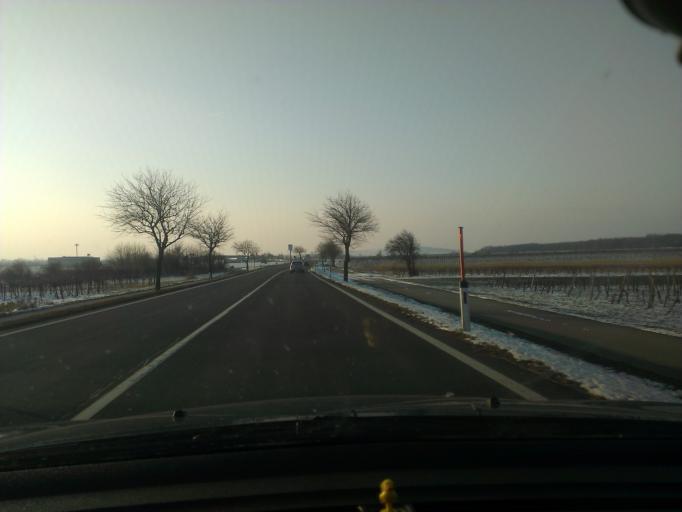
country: AT
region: Burgenland
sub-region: Eisenstadt-Umgebung
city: Donnerskirchen
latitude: 47.8822
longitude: 16.6478
